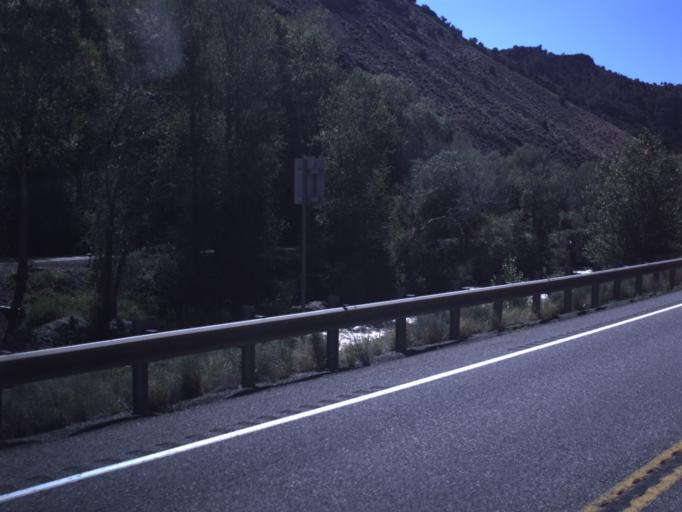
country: US
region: Utah
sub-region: Sevier County
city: Monroe
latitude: 38.5605
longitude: -112.2729
